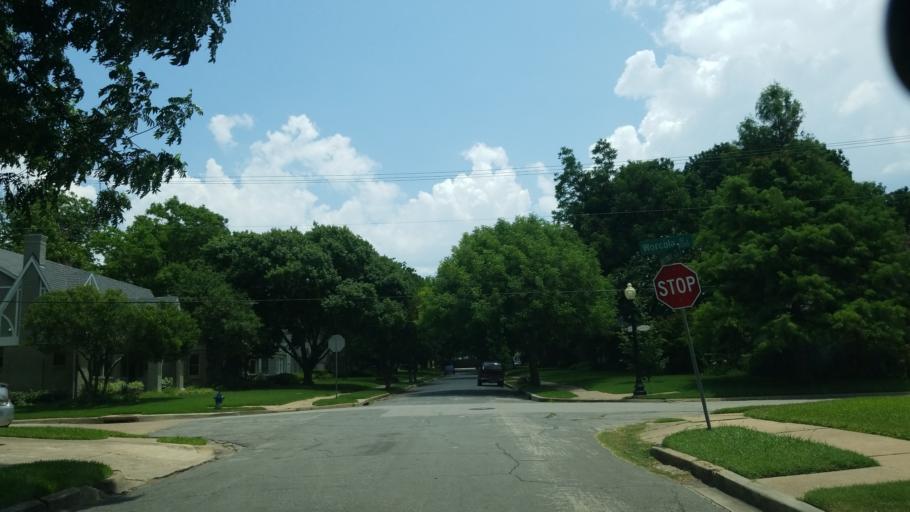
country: US
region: Texas
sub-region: Dallas County
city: Highland Park
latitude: 32.8274
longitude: -96.7726
